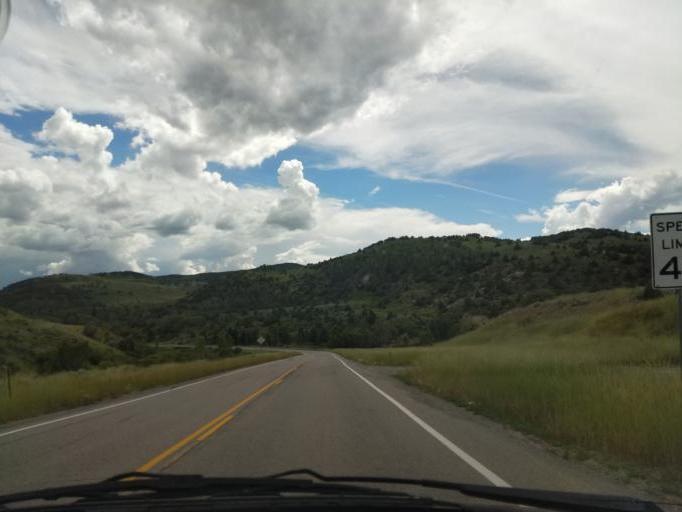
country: US
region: Colorado
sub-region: Delta County
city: Paonia
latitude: 39.0790
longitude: -107.3685
